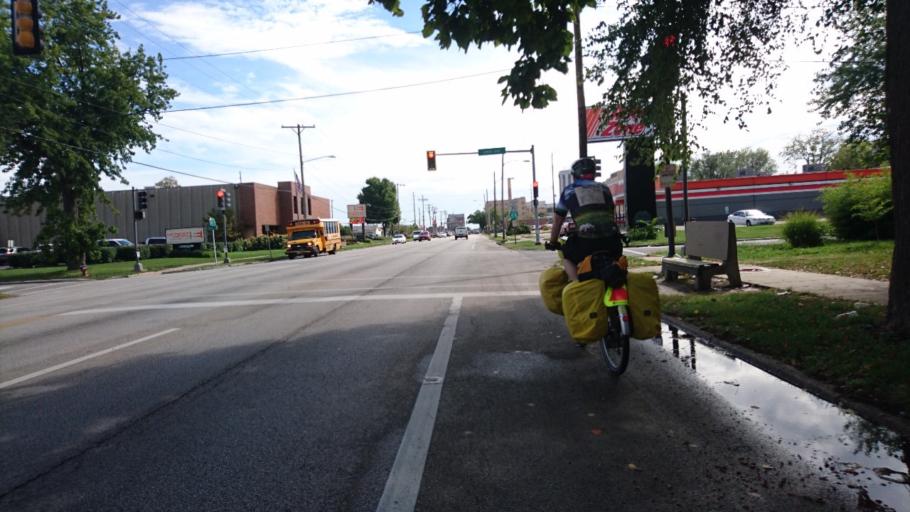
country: US
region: Illinois
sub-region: Sangamon County
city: Springfield
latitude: 39.8099
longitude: -89.6435
